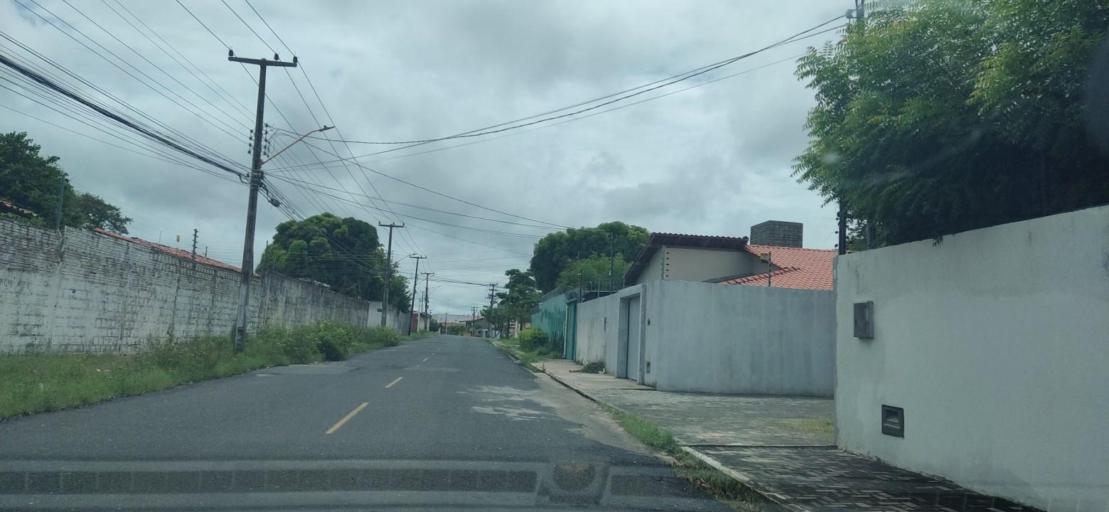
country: BR
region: Piaui
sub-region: Teresina
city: Teresina
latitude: -5.0719
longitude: -42.7634
